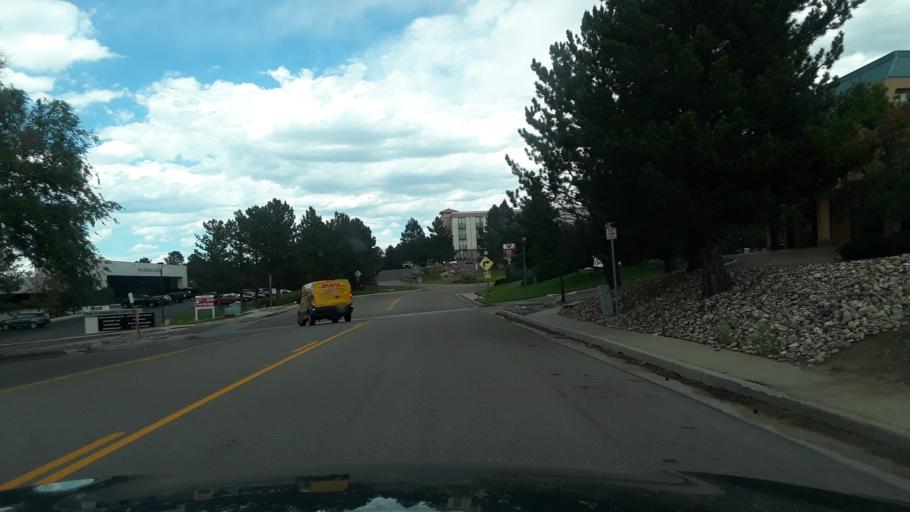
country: US
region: Colorado
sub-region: El Paso County
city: Air Force Academy
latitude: 38.9350
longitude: -104.8152
